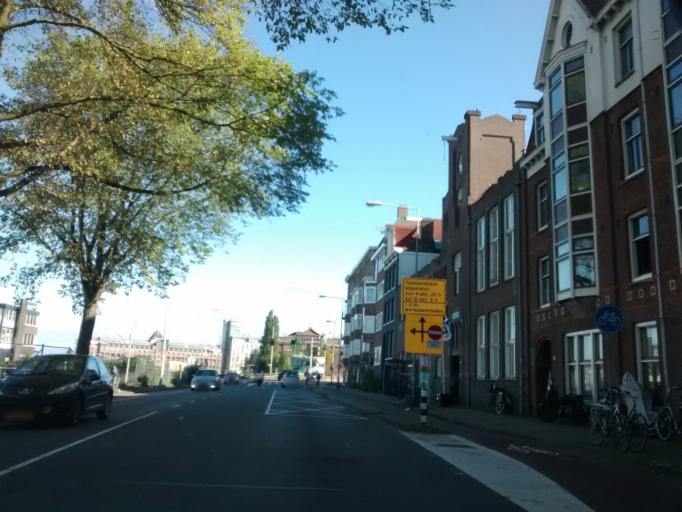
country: NL
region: North Holland
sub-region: Gemeente Amsterdam
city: Amsterdam
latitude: 52.3910
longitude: 4.8833
